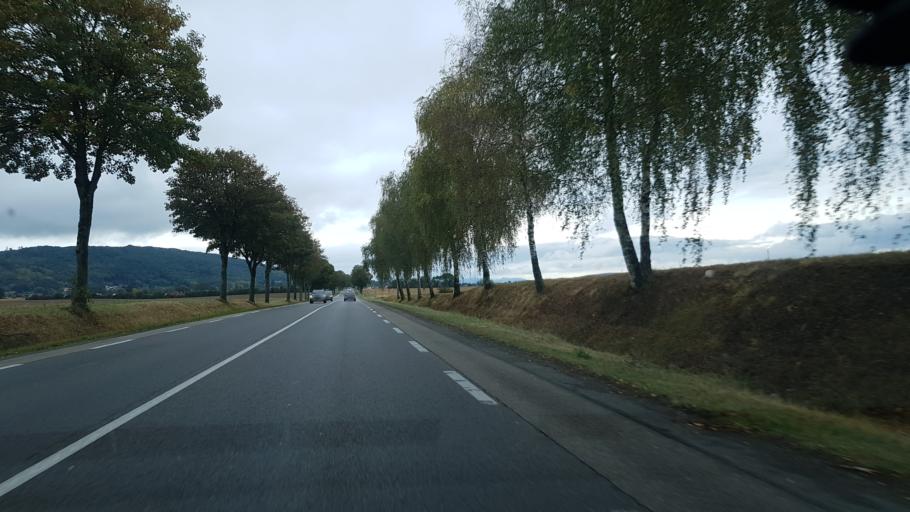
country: FR
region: Rhone-Alpes
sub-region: Departement de l'Ain
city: Saint-Martin-du-Mont
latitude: 46.1125
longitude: 5.3013
